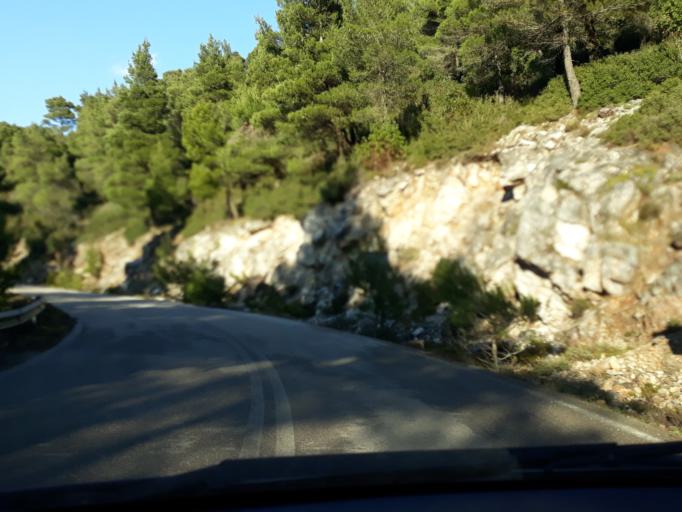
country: GR
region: Attica
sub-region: Nomarchia Dytikis Attikis
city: Fyli
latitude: 38.1548
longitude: 23.6306
